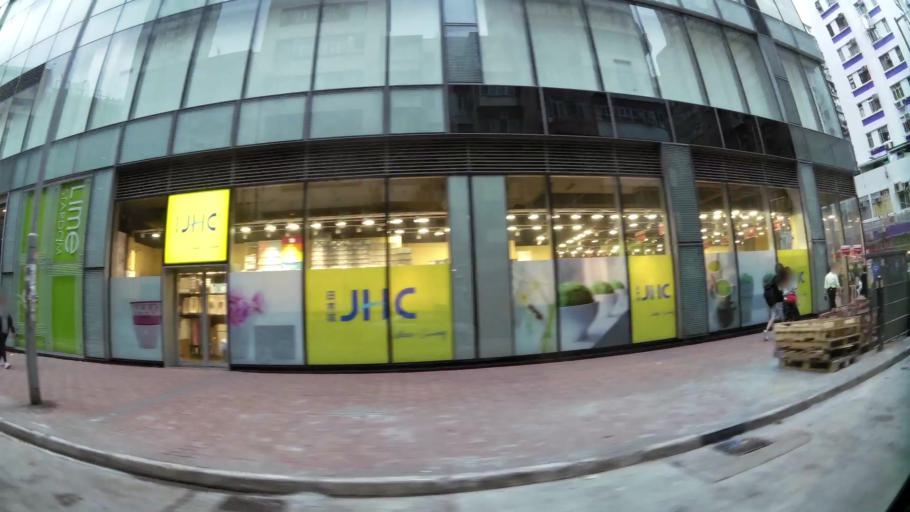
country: HK
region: Sham Shui Po
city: Sham Shui Po
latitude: 22.3213
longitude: 114.1649
